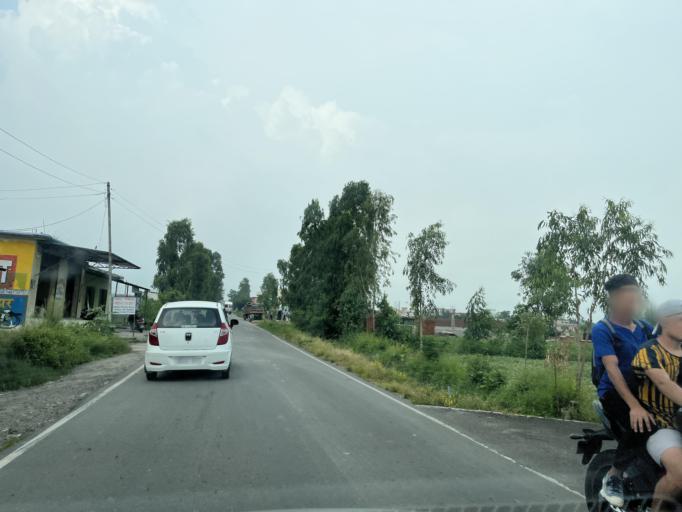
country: IN
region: Uttarakhand
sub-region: Naini Tal
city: Haldwani
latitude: 29.1816
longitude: 79.4741
